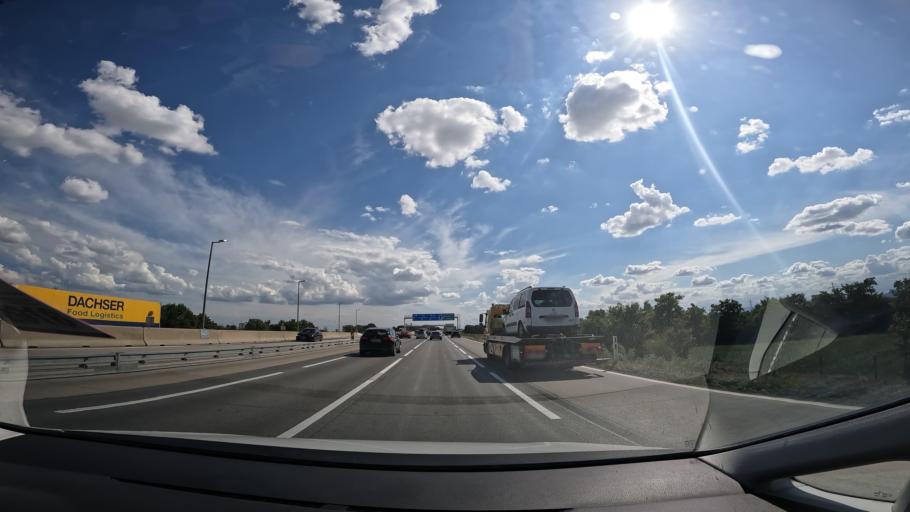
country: AT
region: Lower Austria
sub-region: Politischer Bezirk Modling
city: Laxenburg
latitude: 48.0509
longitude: 16.3399
